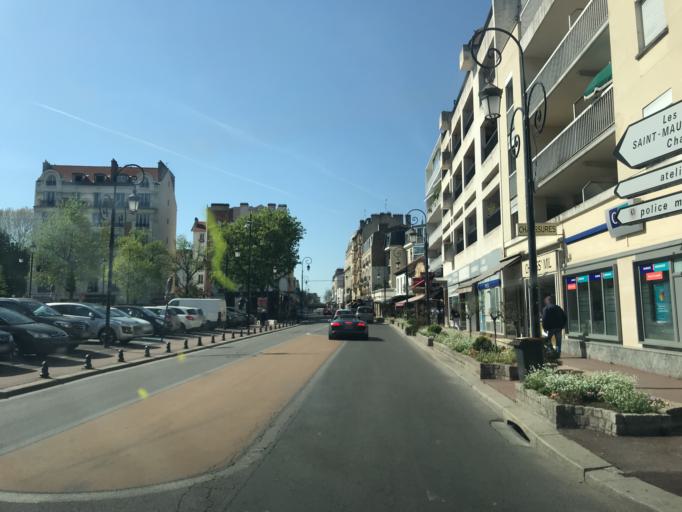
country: FR
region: Ile-de-France
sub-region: Departement du Val-de-Marne
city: Saint-Maur-des-Fosses
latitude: 48.7926
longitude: 2.5169
